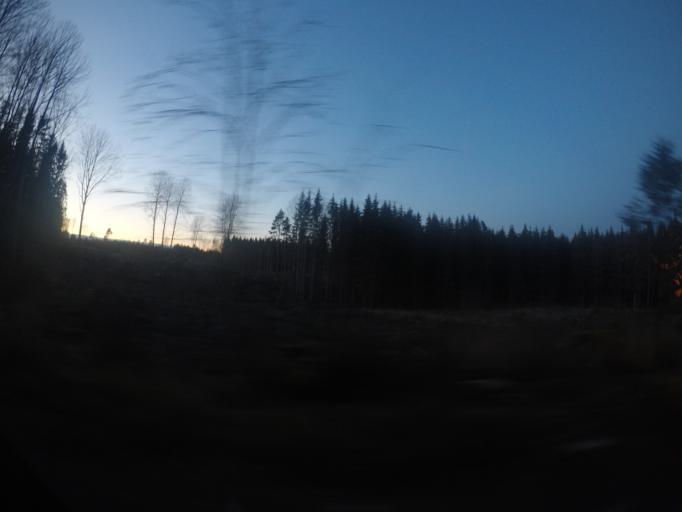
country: SE
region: OErebro
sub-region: Lindesbergs Kommun
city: Fellingsbro
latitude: 59.3543
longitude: 15.5781
